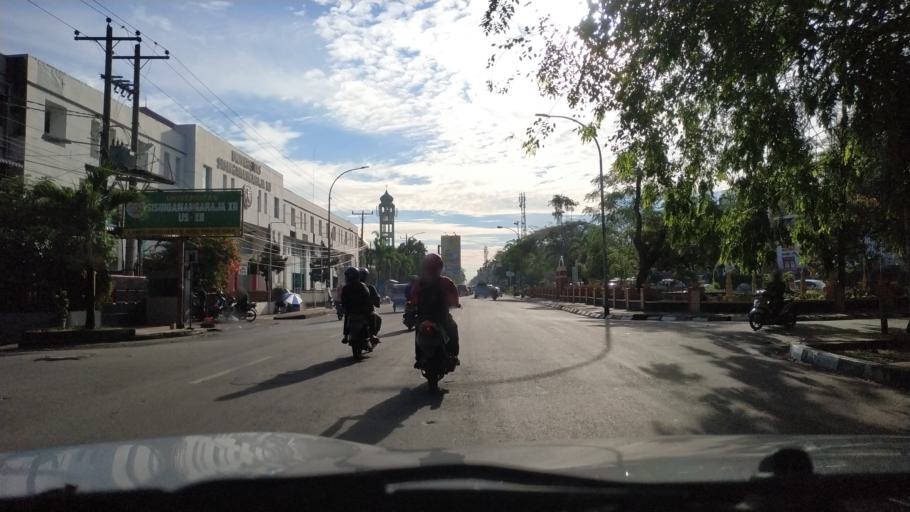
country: ID
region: North Sumatra
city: Medan
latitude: 3.5986
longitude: 98.6903
